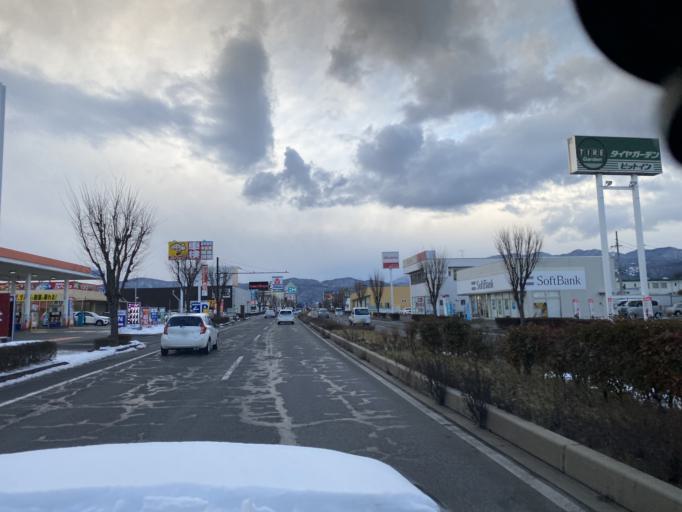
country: JP
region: Nagano
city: Nagano-shi
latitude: 36.6029
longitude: 138.1741
